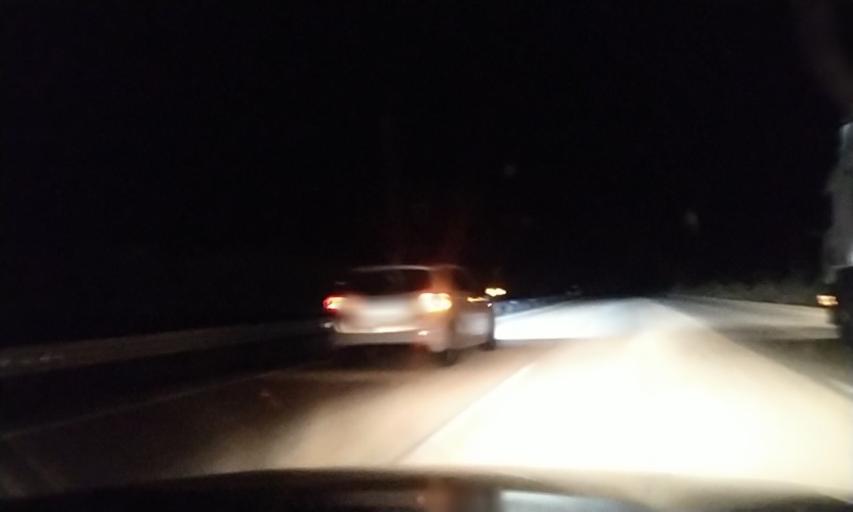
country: ES
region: Castille and Leon
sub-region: Provincia de Zamora
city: Requejo
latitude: 42.0401
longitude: -6.7767
